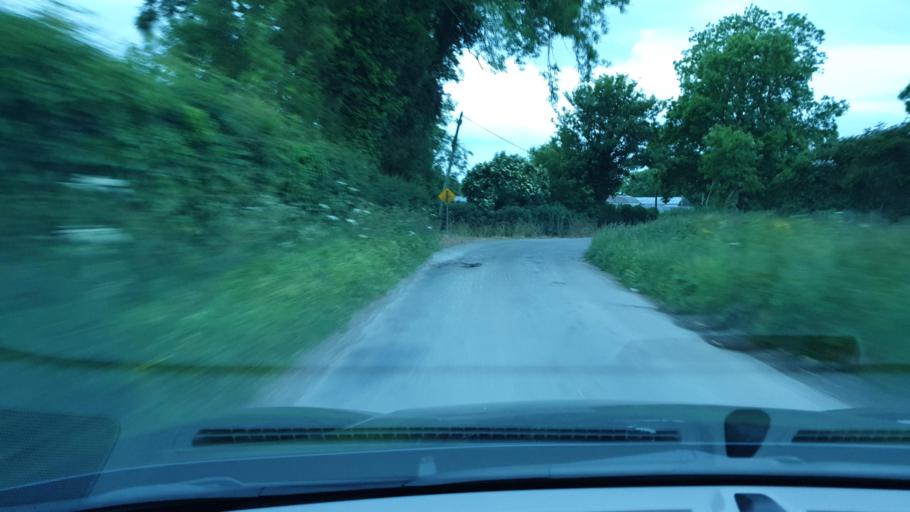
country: IE
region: Leinster
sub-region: An Mhi
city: Duleek
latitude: 53.6054
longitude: -6.3715
